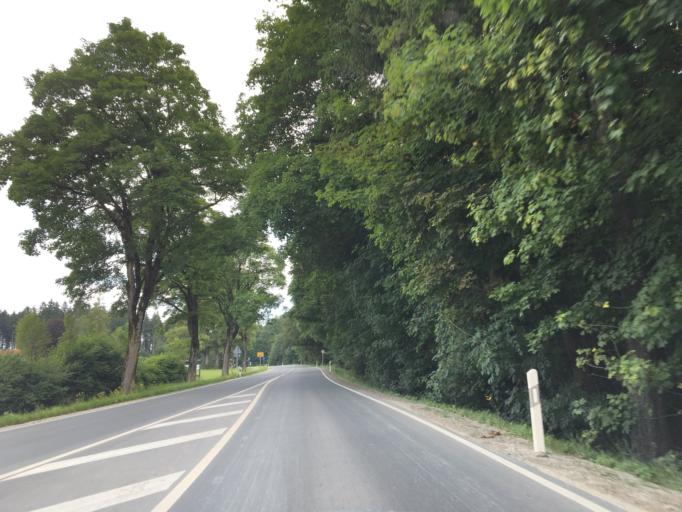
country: DE
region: Bavaria
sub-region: Upper Bavaria
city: Holzkirchen
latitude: 47.8889
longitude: 11.6850
